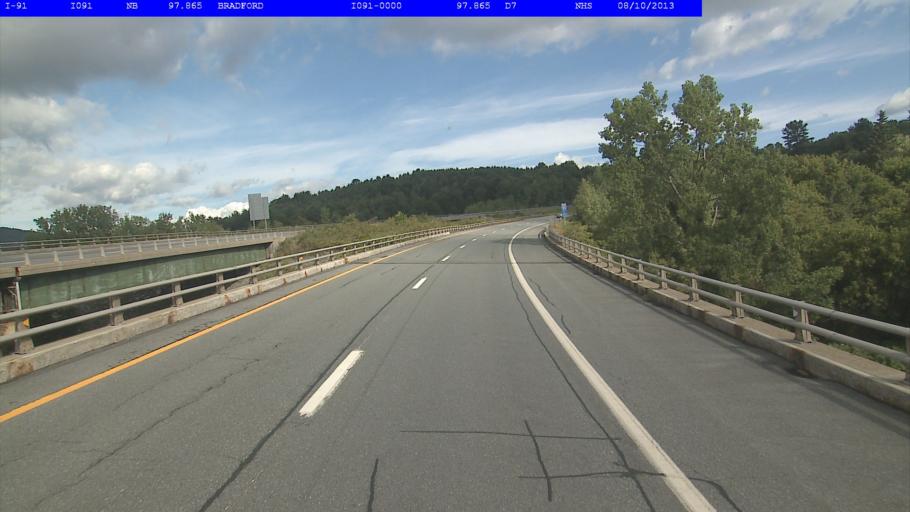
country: US
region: New Hampshire
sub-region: Grafton County
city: Orford
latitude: 43.9862
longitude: -72.1340
